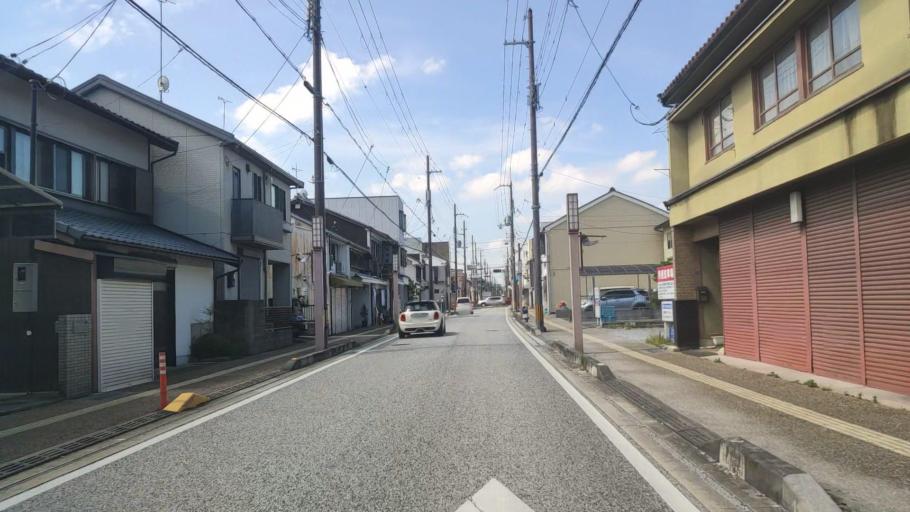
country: JP
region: Shiga Prefecture
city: Hikone
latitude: 35.2707
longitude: 136.2591
